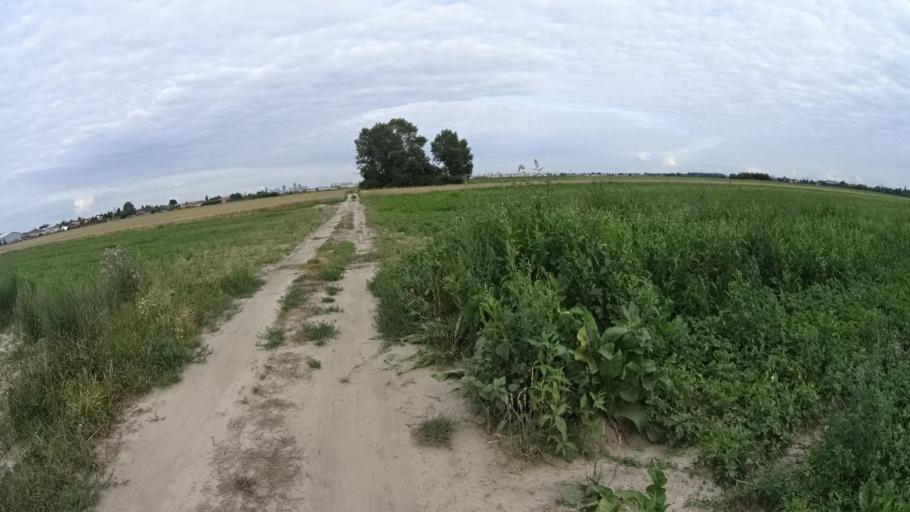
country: PL
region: Masovian Voivodeship
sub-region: Powiat warszawski zachodni
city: Babice
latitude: 52.2403
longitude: 20.8608
